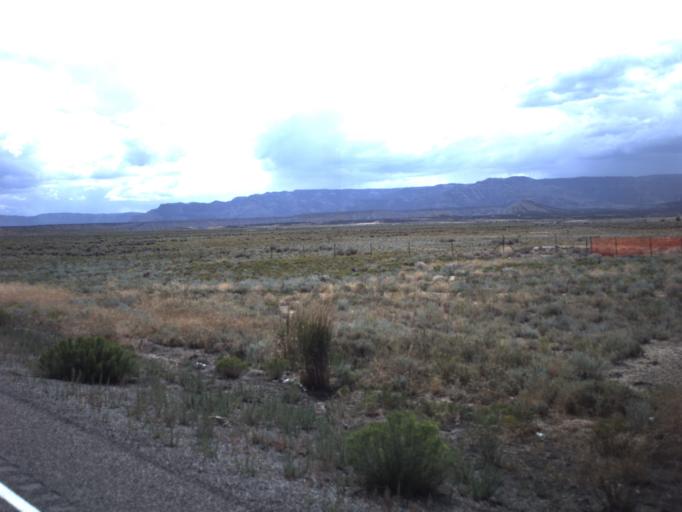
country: US
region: Utah
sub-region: Carbon County
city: Price
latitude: 39.4960
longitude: -110.8437
